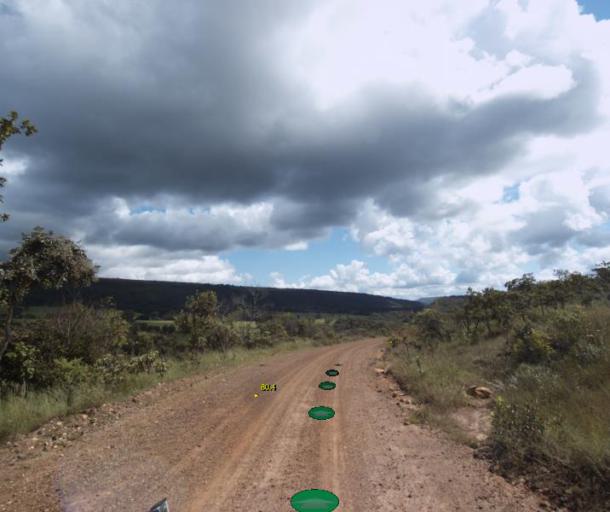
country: BR
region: Goias
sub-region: Pirenopolis
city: Pirenopolis
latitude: -15.7869
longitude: -48.8661
